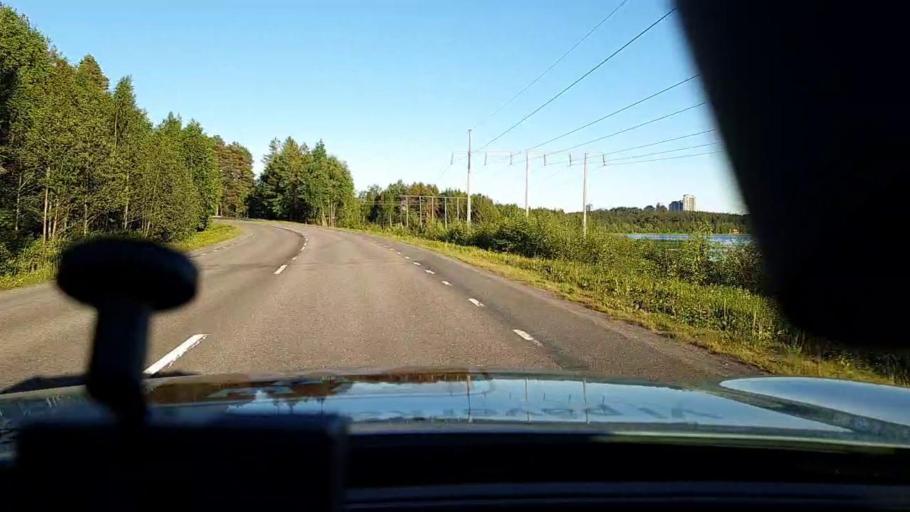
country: SE
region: Norrbotten
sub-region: Lulea Kommun
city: Lulea
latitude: 65.6083
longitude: 22.1685
